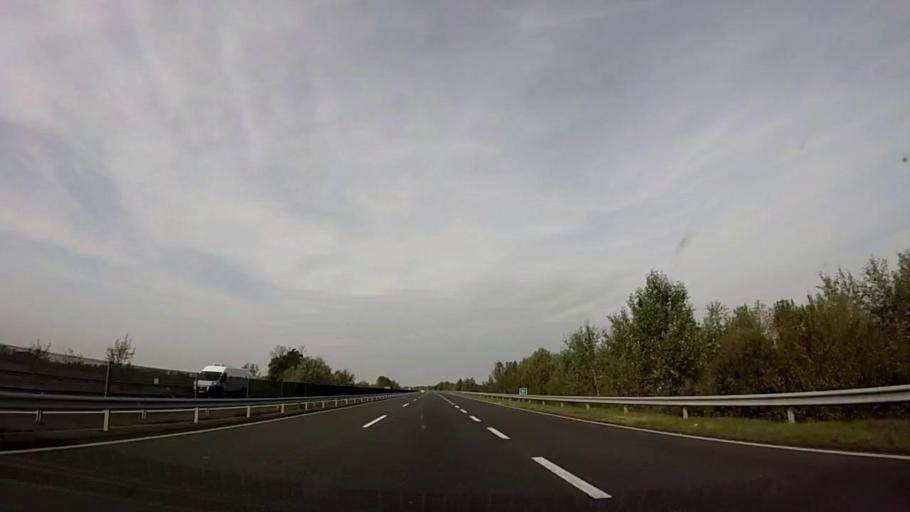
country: HU
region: Somogy
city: Balatonfenyves
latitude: 46.7003
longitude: 17.5102
